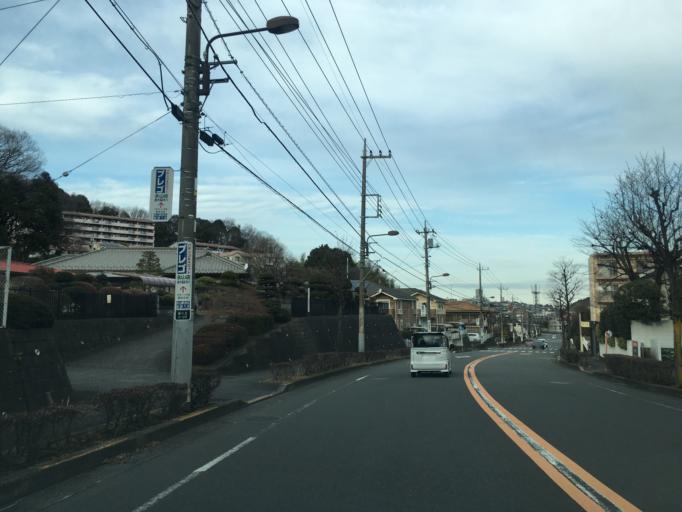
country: JP
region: Tokyo
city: Hino
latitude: 35.6252
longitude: 139.4371
